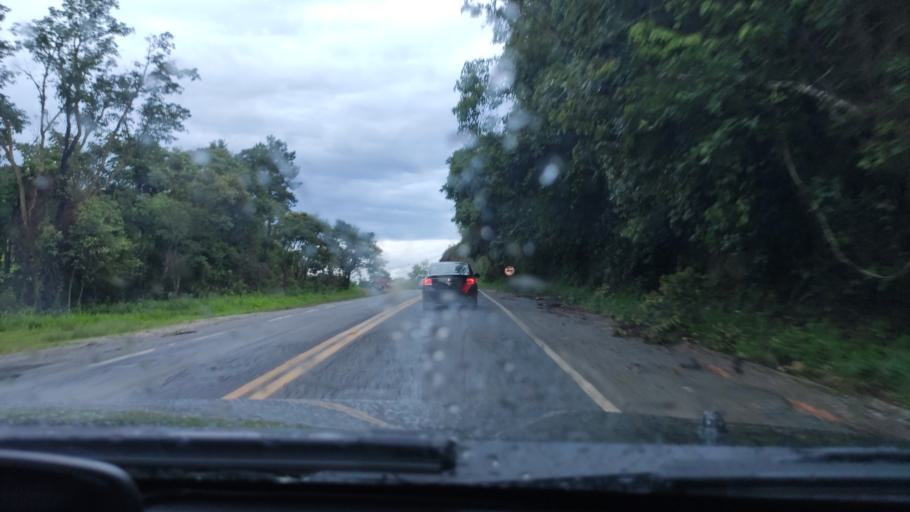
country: BR
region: Sao Paulo
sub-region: Braganca Paulista
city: Braganca Paulista
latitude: -22.7861
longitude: -46.5597
